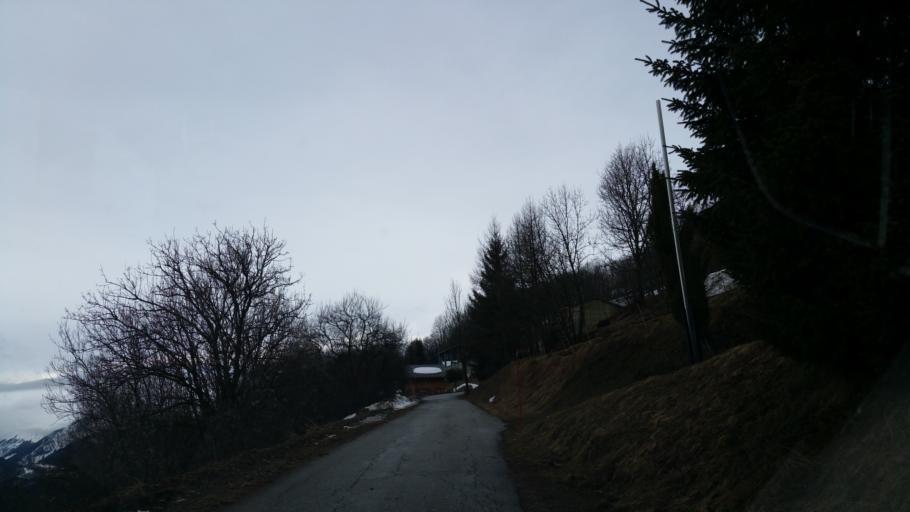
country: FR
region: Rhone-Alpes
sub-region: Departement de la Savoie
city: Villargondran
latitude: 45.2819
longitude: 6.4040
